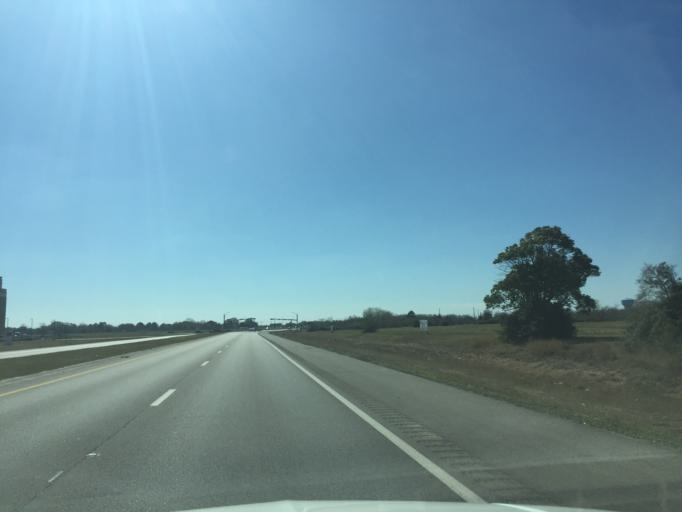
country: US
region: Texas
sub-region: Galveston County
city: Kemah
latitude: 29.5170
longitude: -95.0252
